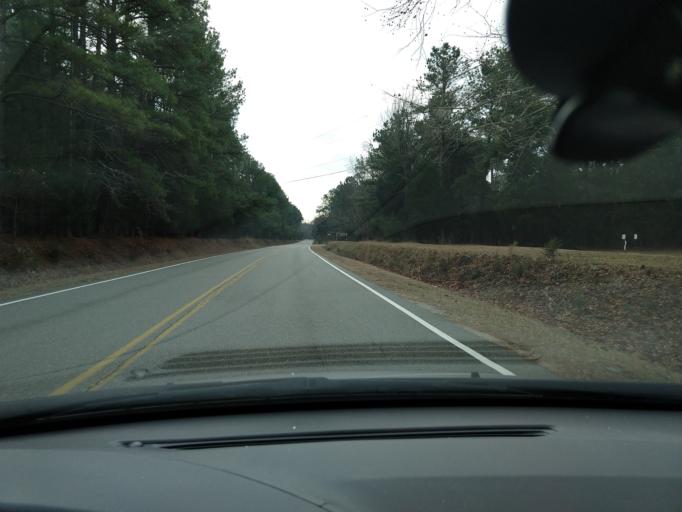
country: US
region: Virginia
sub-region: Henrico County
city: Fort Lee
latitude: 37.4331
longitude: -77.3661
